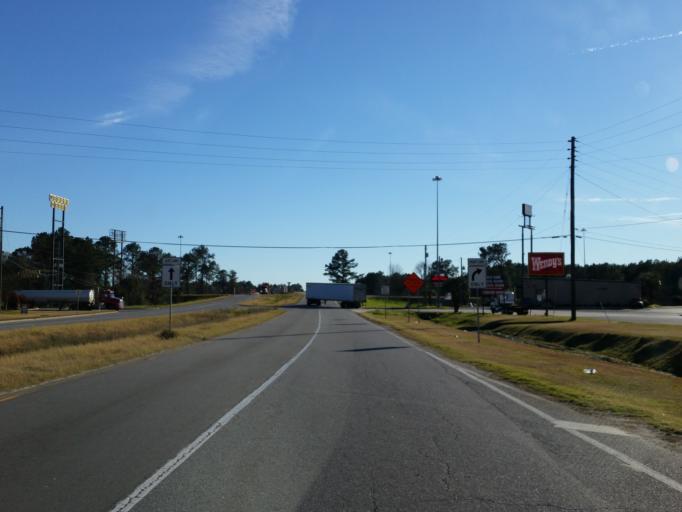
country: US
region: Georgia
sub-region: Lowndes County
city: Valdosta
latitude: 30.7539
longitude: -83.2724
